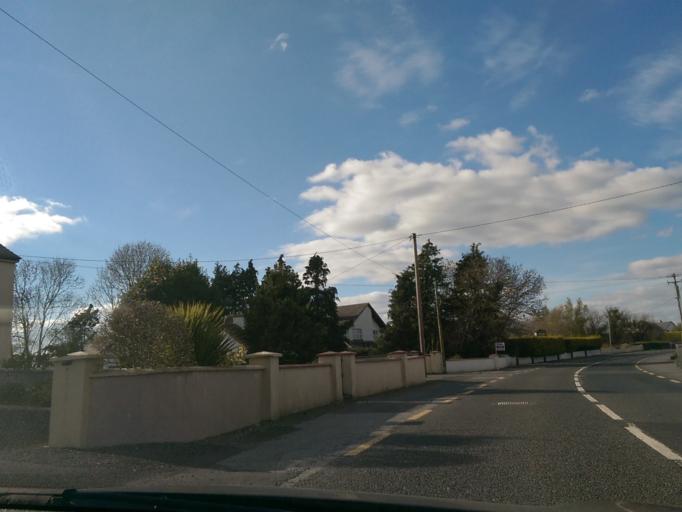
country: IE
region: Connaught
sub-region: County Galway
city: Portumna
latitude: 53.1054
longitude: -8.2355
